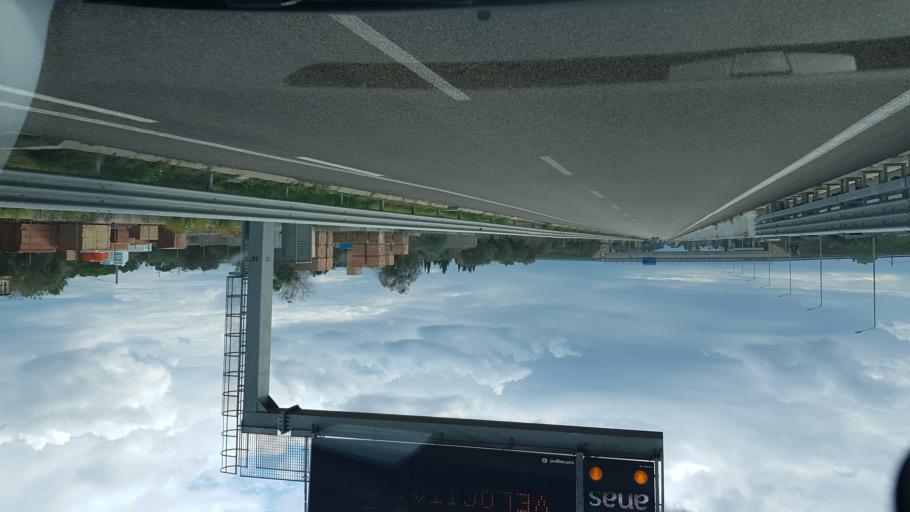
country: IT
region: Apulia
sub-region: Provincia di Lecce
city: Muro Leccese
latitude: 40.1253
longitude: 18.3402
